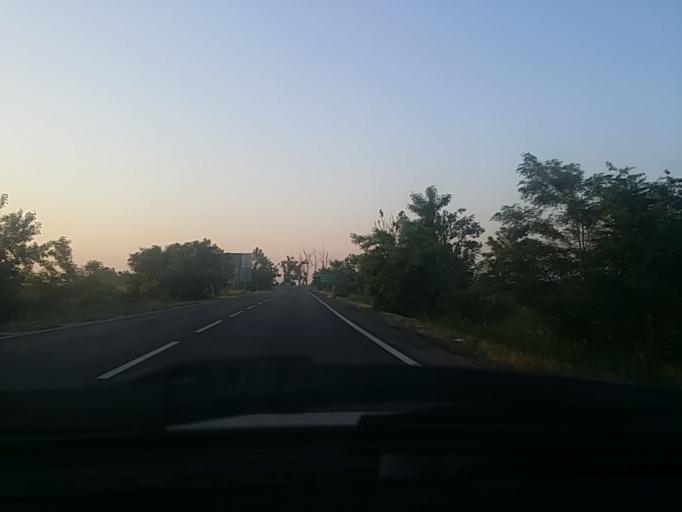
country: HU
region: Pest
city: Ecser
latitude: 47.4633
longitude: 19.3363
